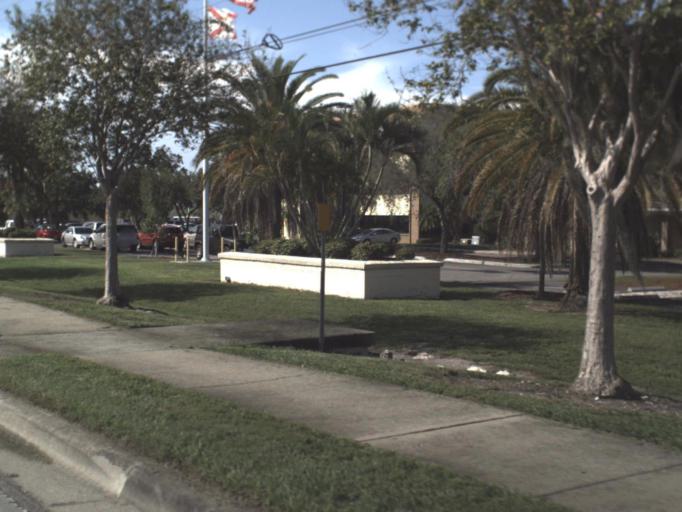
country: US
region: Florida
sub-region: Sarasota County
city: South Sarasota
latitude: 27.2799
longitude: -82.5309
